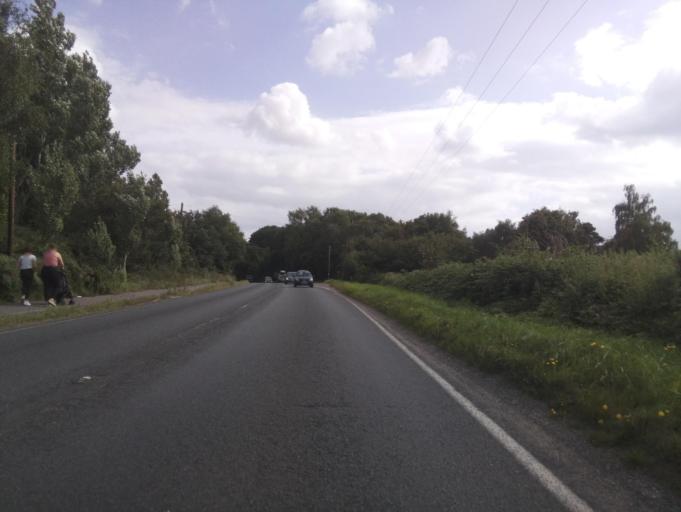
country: GB
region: England
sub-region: Hampshire
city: Marchwood
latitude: 50.8680
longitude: -1.4385
